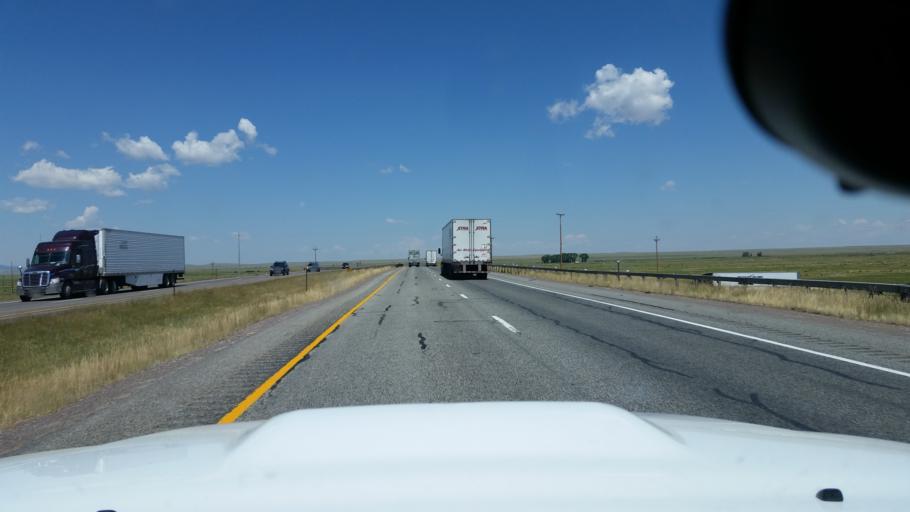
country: US
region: Wyoming
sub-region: Albany County
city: Laramie
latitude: 41.3934
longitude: -105.8228
